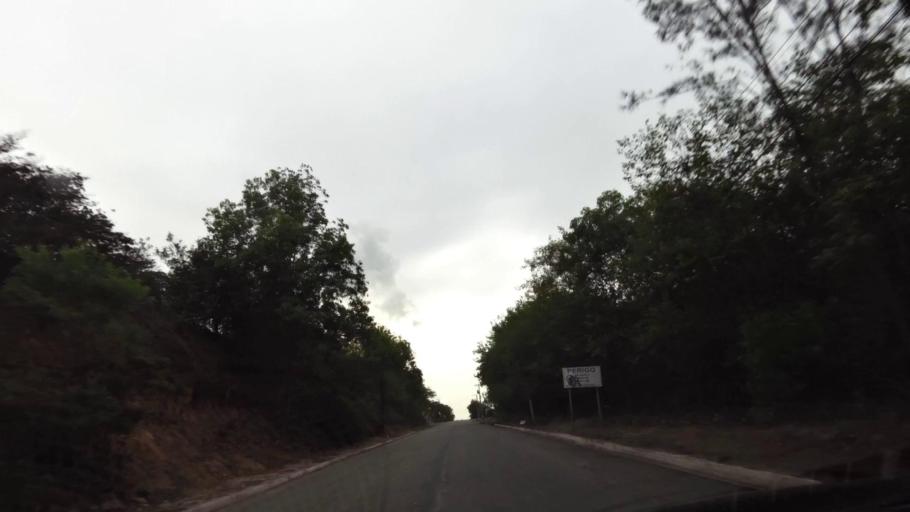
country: BR
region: Espirito Santo
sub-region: Piuma
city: Piuma
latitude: -20.7930
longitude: -40.5814
